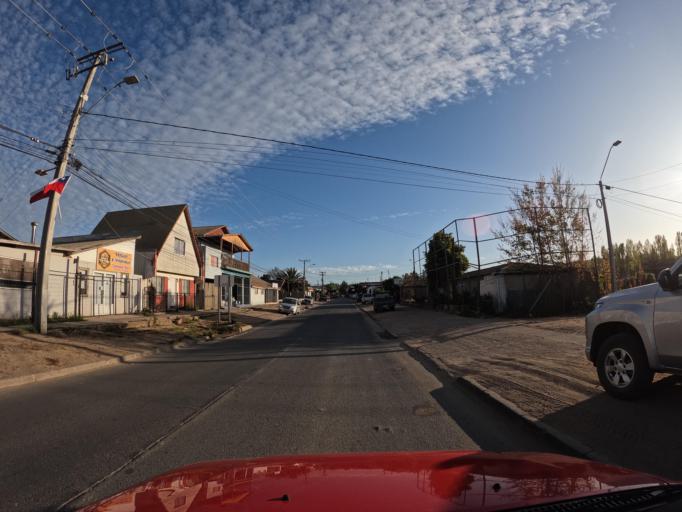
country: CL
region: Valparaiso
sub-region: San Antonio Province
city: San Antonio
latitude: -34.1134
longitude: -71.7257
